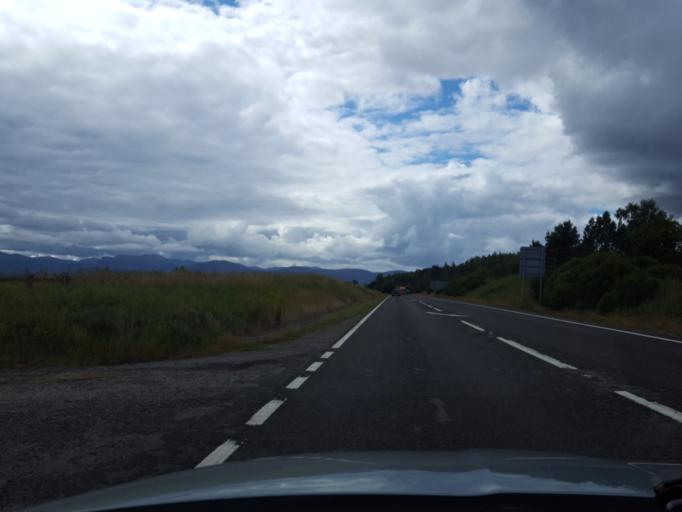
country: GB
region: Scotland
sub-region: Highland
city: Grantown on Spey
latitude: 57.2979
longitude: -3.6622
